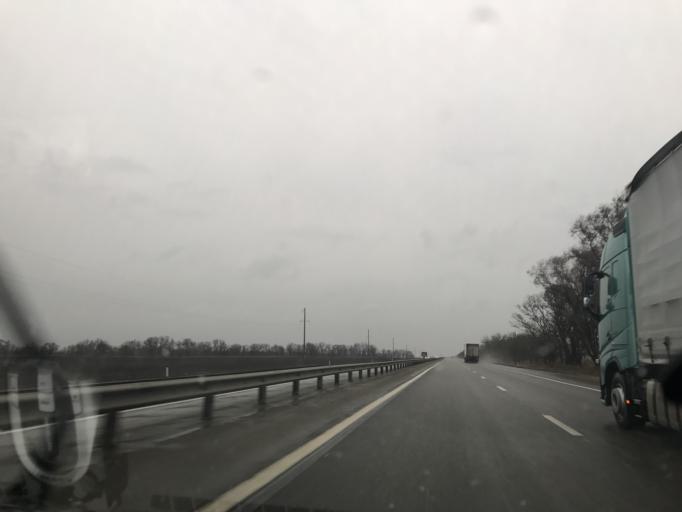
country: RU
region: Krasnodarskiy
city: Kislyakovskaya
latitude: 46.3928
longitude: 39.7357
